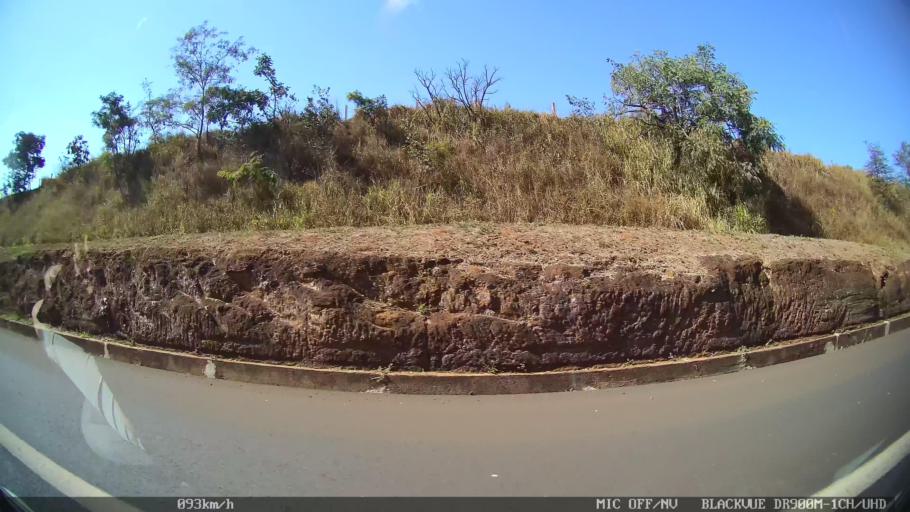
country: BR
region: Sao Paulo
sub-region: Batatais
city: Batatais
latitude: -20.7389
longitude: -47.5308
